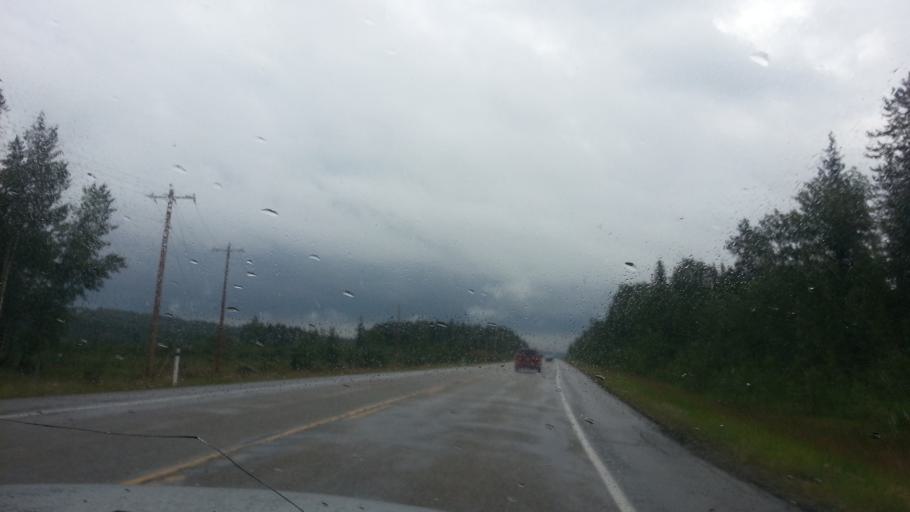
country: CA
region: Alberta
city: Cochrane
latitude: 50.9214
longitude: -114.6001
